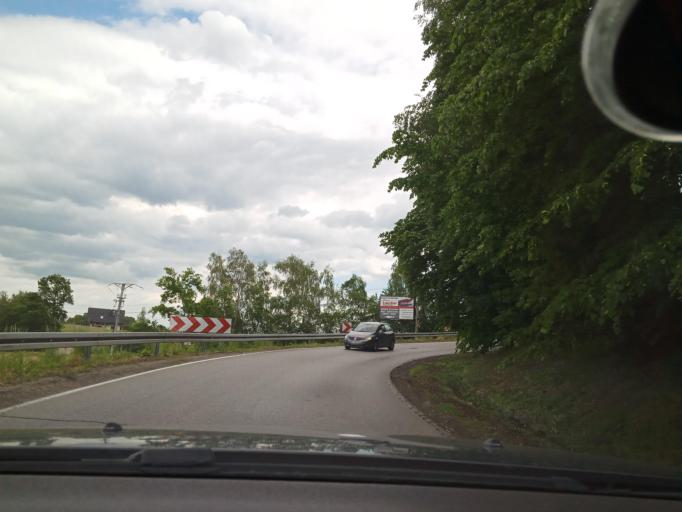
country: PL
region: Lesser Poland Voivodeship
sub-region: Powiat bochenski
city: Lapanow
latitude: 49.8111
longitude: 20.3178
